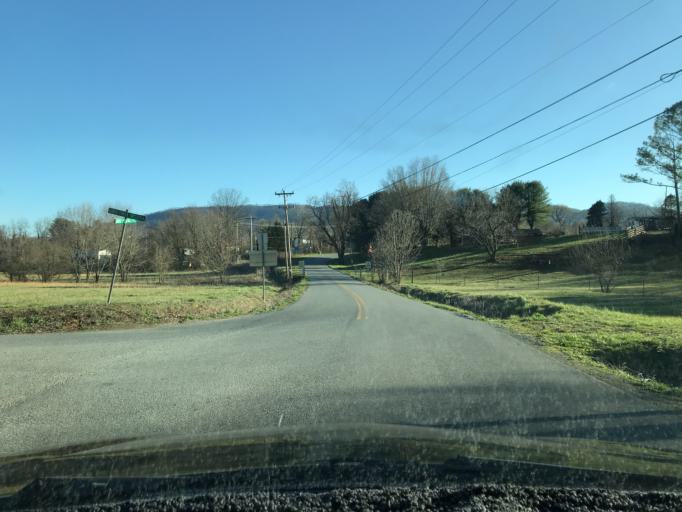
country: US
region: Virginia
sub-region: Botetourt County
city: Blue Ridge
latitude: 37.3905
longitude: -79.7259
